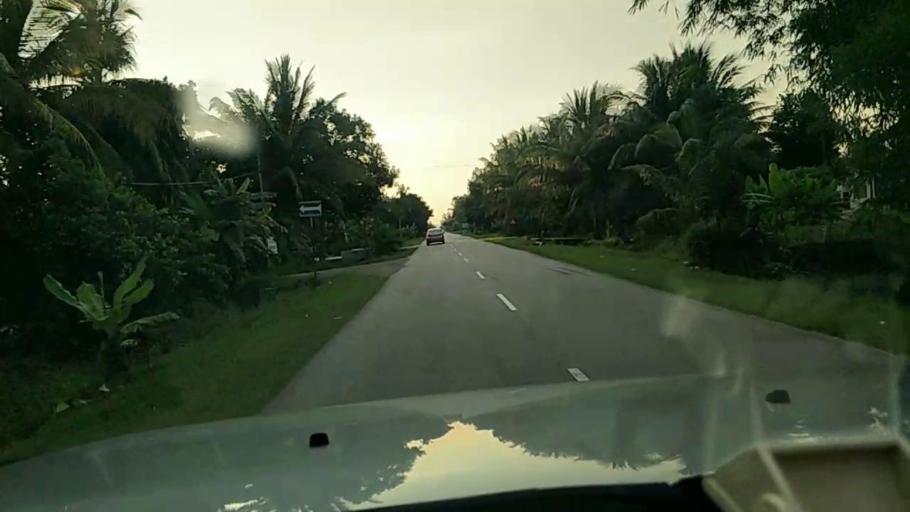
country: MY
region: Selangor
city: Kuala Selangor
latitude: 3.3072
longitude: 101.2927
